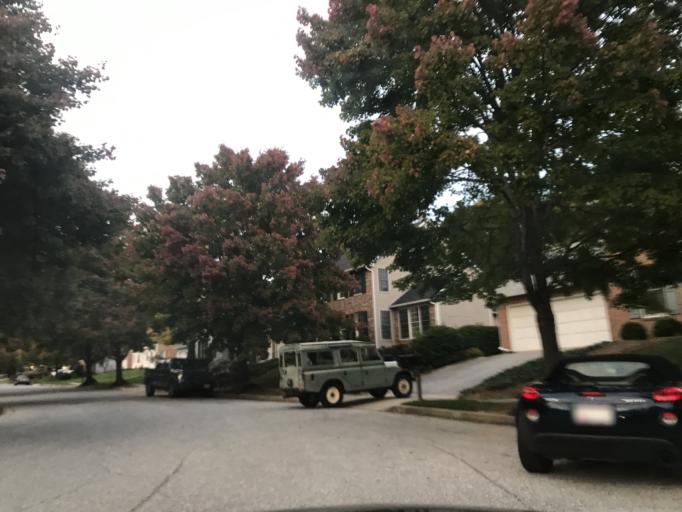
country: US
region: Maryland
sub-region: Baltimore County
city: Lutherville
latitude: 39.4088
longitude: -76.6302
